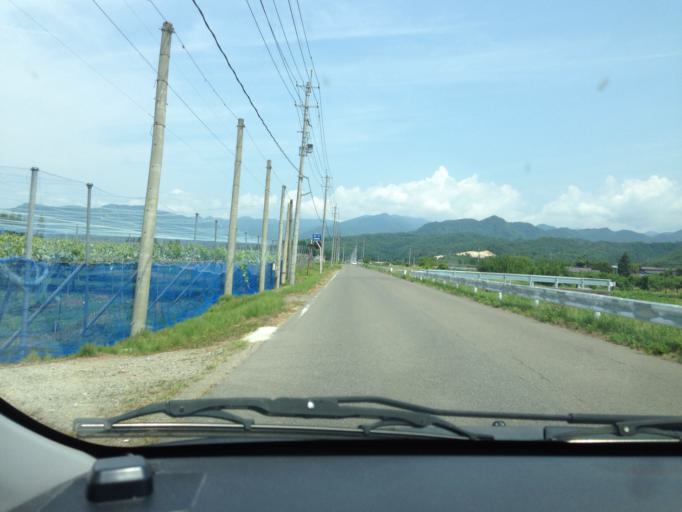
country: JP
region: Fukushima
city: Kitakata
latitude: 37.6814
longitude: 139.8819
